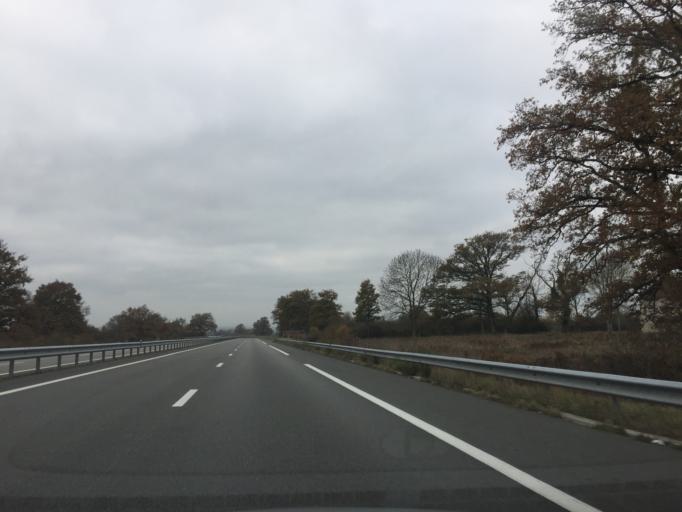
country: FR
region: Limousin
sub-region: Departement de la Creuse
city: Gouzon
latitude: 46.2287
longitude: 2.3078
